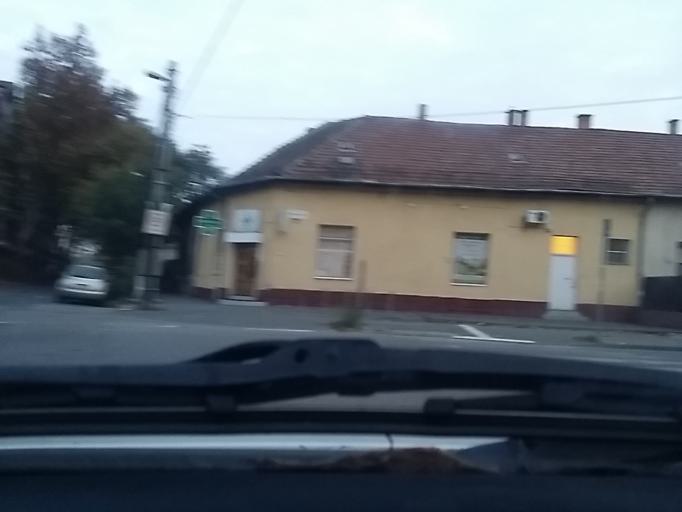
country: HU
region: Budapest
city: Budapest XIV. keruelet
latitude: 47.5309
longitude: 19.1216
